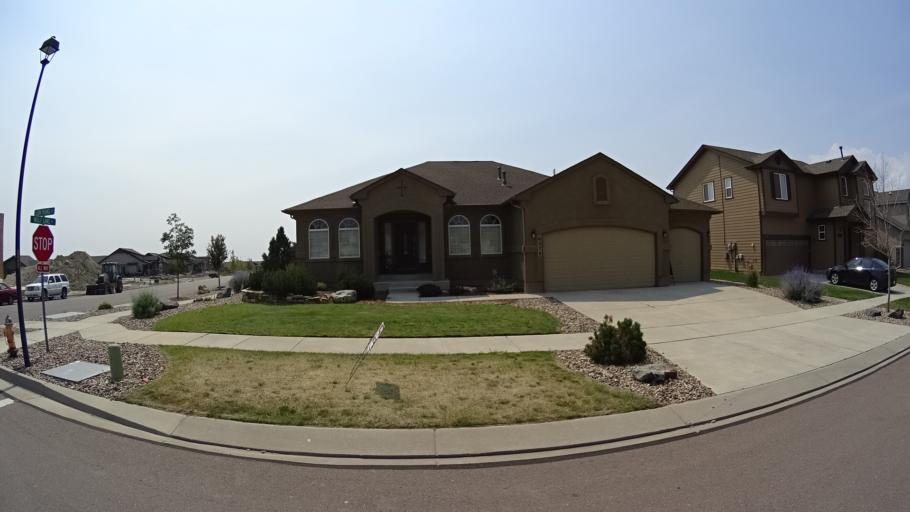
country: US
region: Colorado
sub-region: El Paso County
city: Black Forest
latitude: 38.9702
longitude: -104.7162
